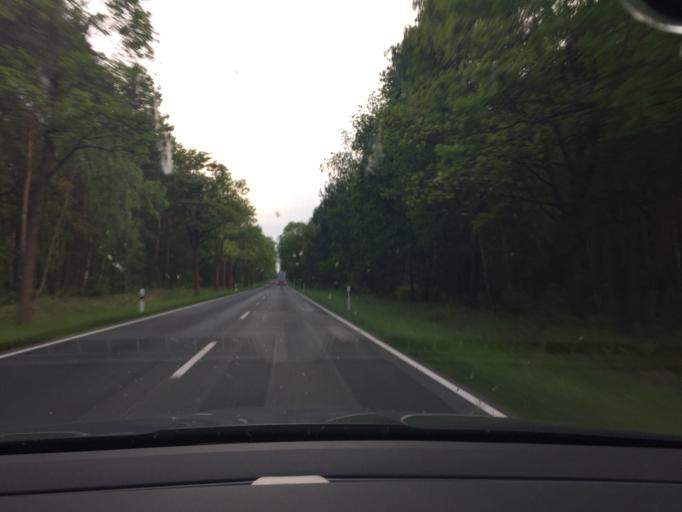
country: DE
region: Brandenburg
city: Treuenbrietzen
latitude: 52.0573
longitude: 12.8223
